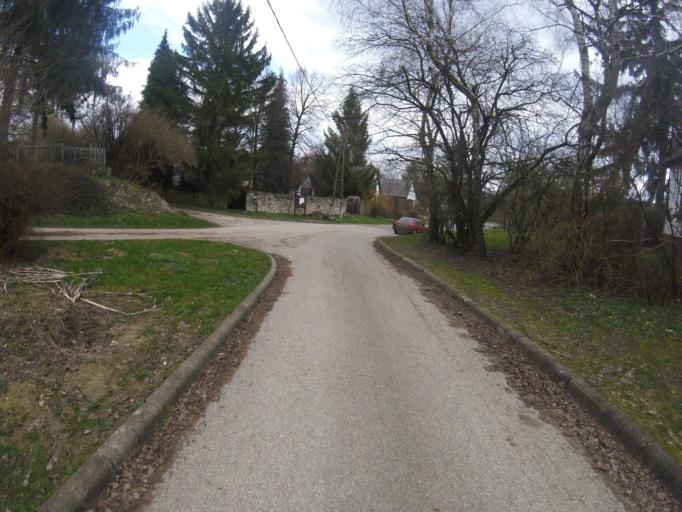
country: HU
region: Fejer
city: Csakvar
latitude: 47.4574
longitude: 18.4326
